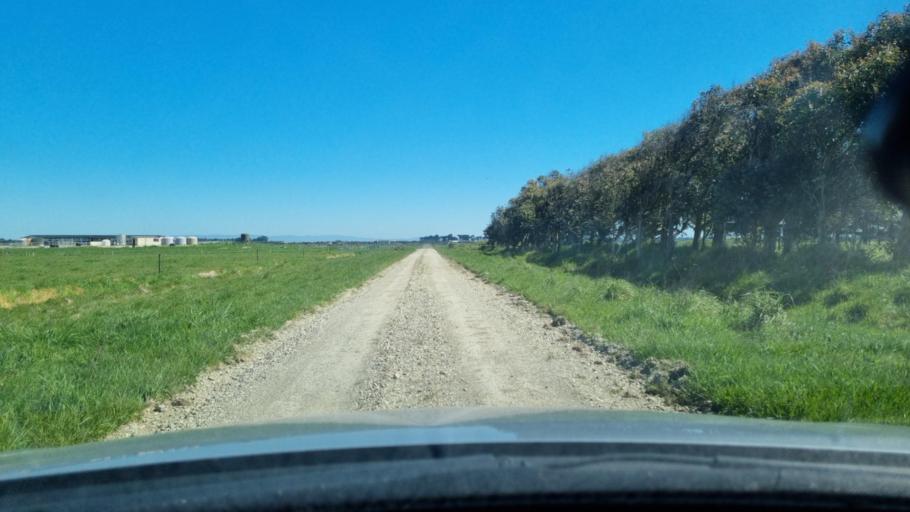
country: NZ
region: Southland
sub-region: Invercargill City
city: Invercargill
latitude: -46.4227
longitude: 168.3132
